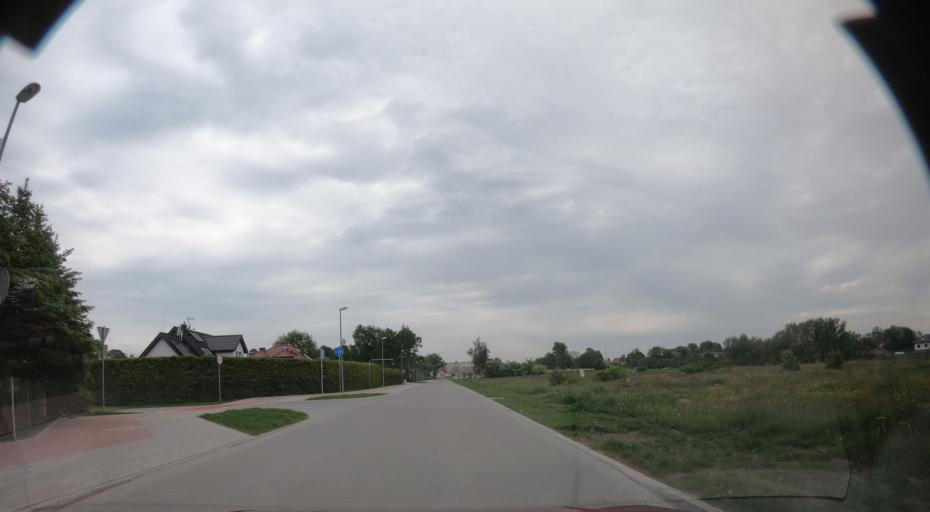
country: PL
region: West Pomeranian Voivodeship
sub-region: Powiat kolobrzeski
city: Kolobrzeg
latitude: 54.1494
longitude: 15.5569
